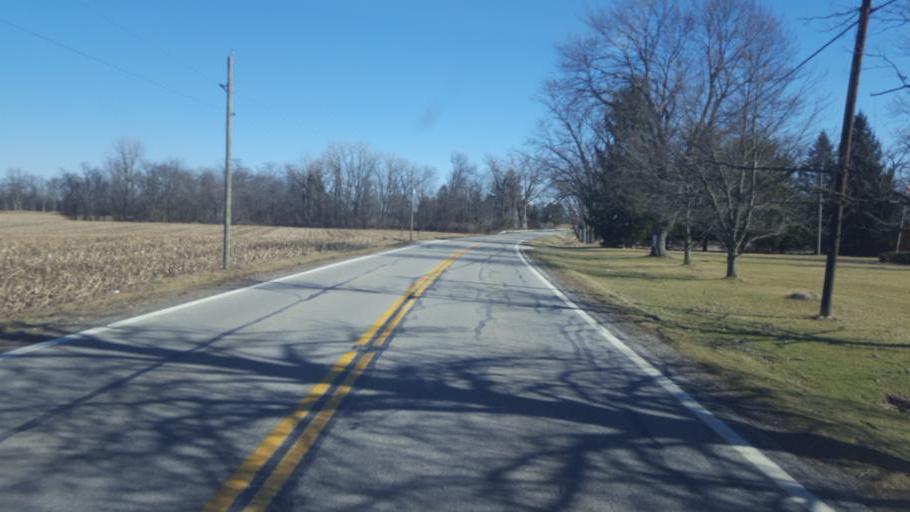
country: US
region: Ohio
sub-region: Marion County
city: Marion
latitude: 40.6122
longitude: -83.1861
